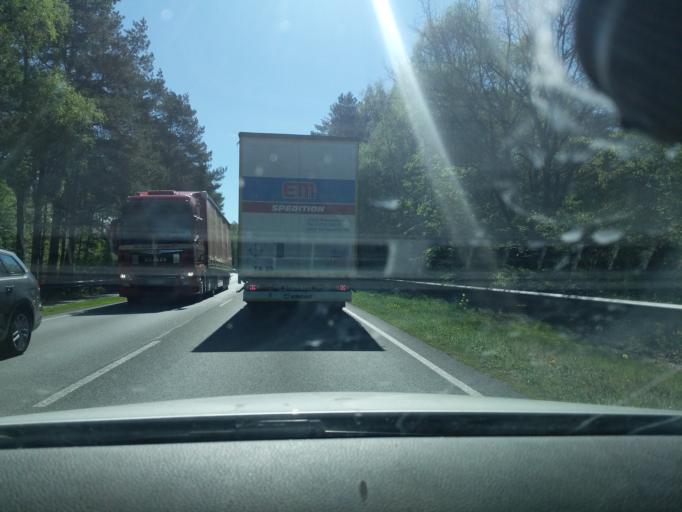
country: DE
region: Lower Saxony
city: Buxtehude
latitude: 53.4559
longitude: 9.7263
